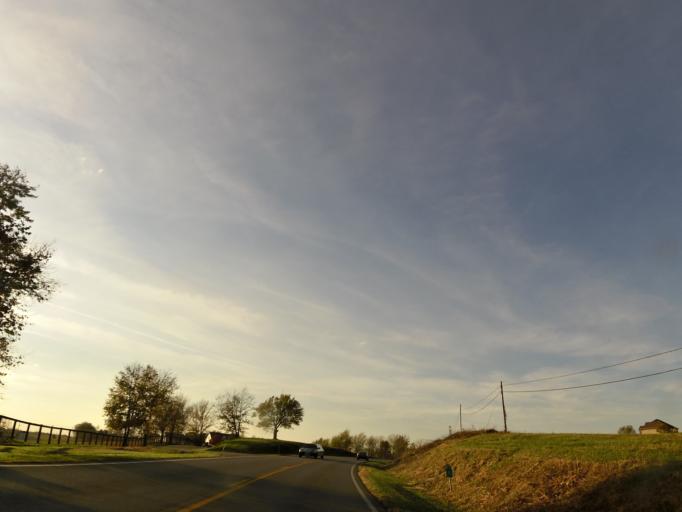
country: US
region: Kentucky
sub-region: Garrard County
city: Lancaster
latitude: 37.6423
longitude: -84.5928
